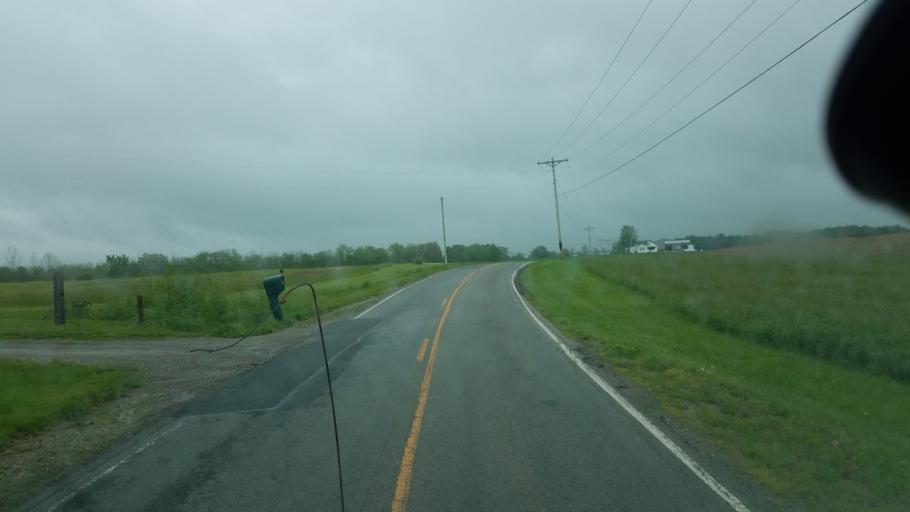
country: US
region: Ohio
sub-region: Highland County
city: Greenfield
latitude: 39.3397
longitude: -83.4505
